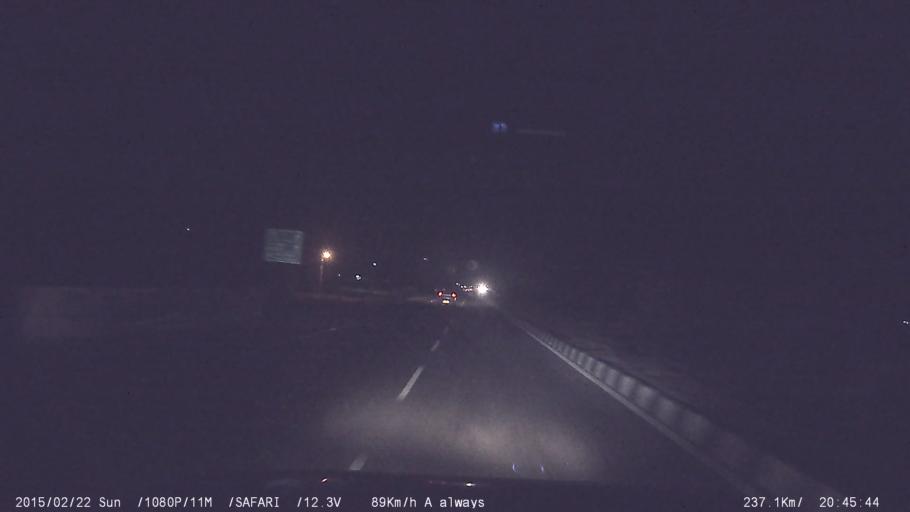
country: IN
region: Tamil Nadu
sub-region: Dindigul
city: Vedasandur
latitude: 10.4730
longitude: 77.9482
